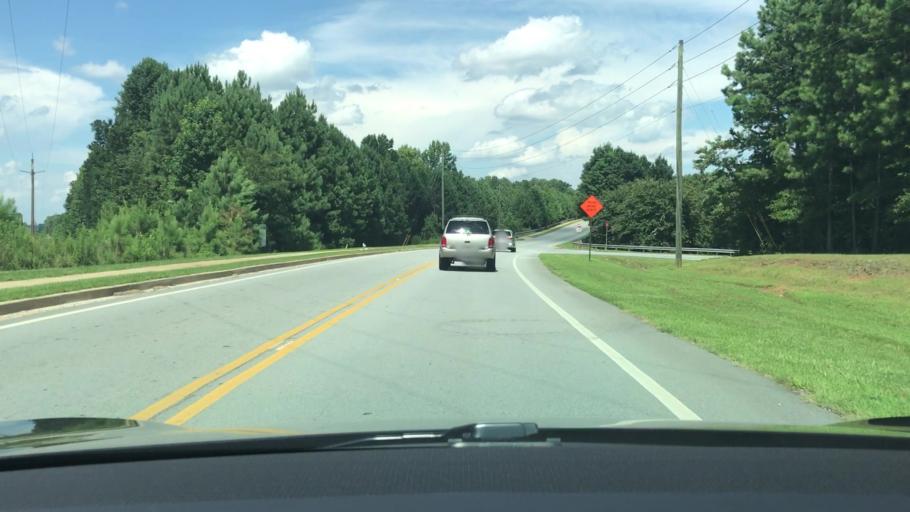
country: US
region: Georgia
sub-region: Gwinnett County
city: Sugar Hill
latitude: 34.0815
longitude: -84.0514
